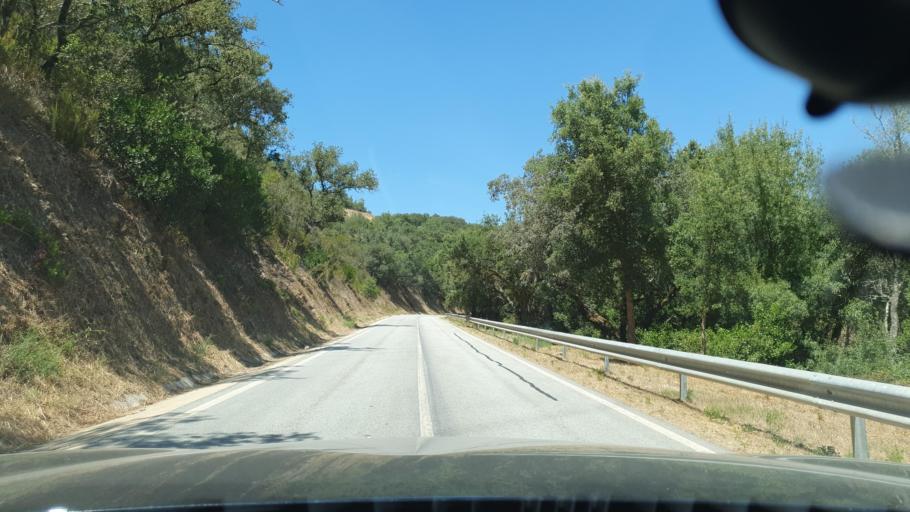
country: PT
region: Beja
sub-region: Odemira
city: Odemira
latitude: 37.5646
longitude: -8.4870
